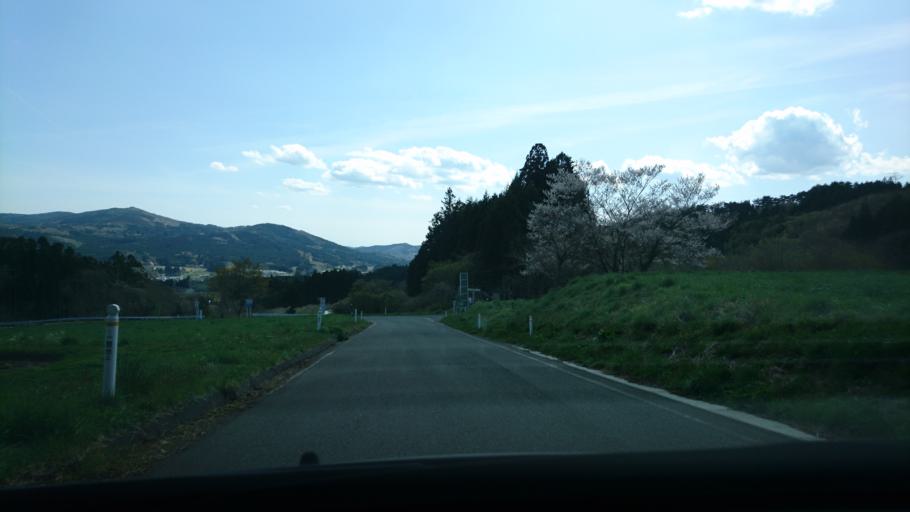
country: JP
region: Iwate
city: Ofunato
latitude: 38.9541
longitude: 141.4517
